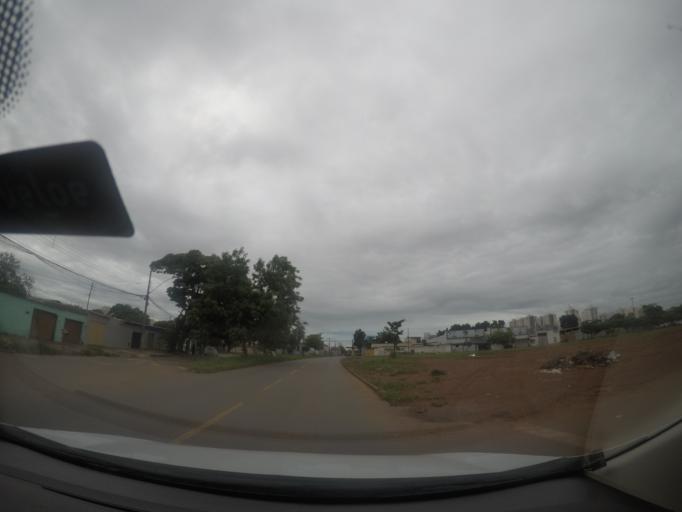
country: BR
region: Goias
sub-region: Goiania
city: Goiania
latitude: -16.6988
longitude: -49.3234
